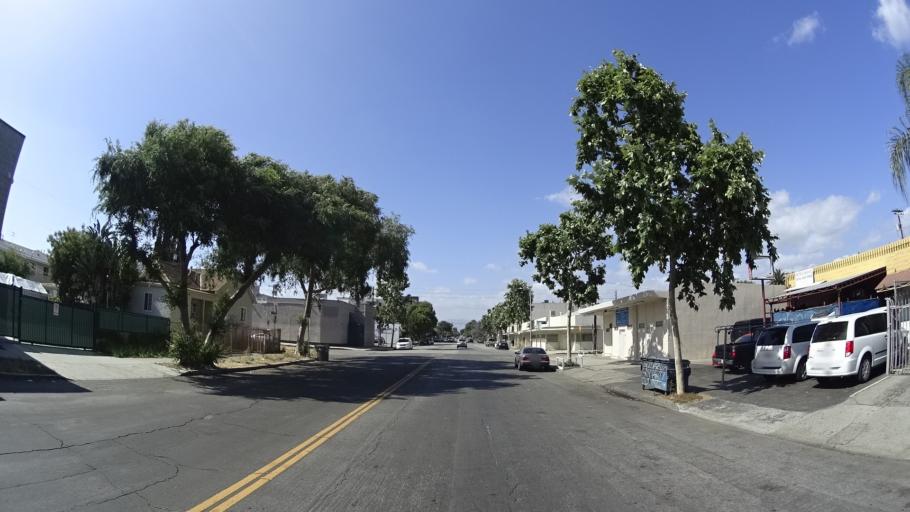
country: US
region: California
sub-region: Los Angeles County
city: North Hollywood
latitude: 34.1746
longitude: -118.3790
